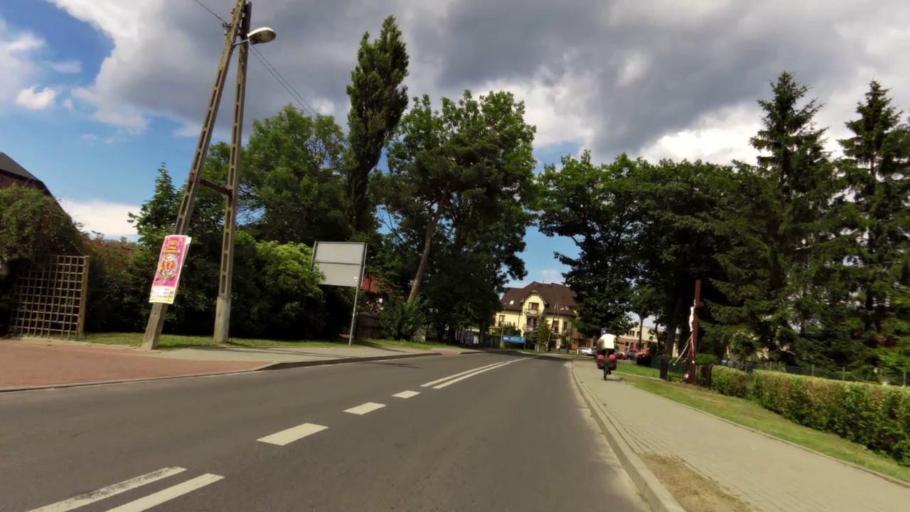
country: PL
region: West Pomeranian Voivodeship
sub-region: Powiat gryficki
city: Mrzezyno
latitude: 54.1419
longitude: 15.2883
